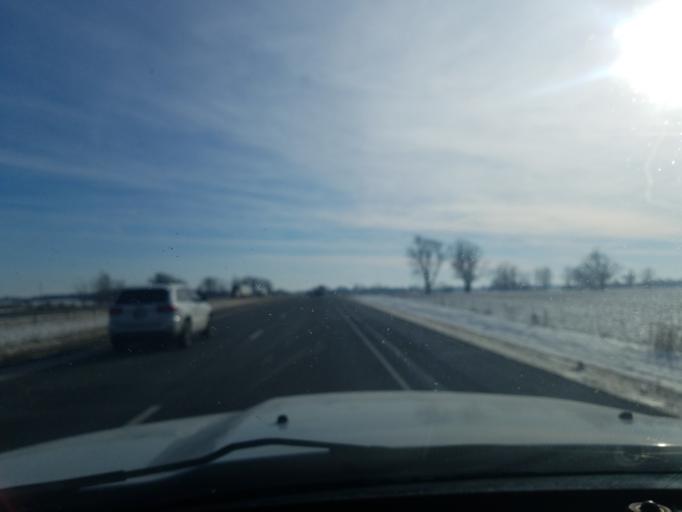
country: US
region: Indiana
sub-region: Grant County
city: Fairmount
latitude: 40.3447
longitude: -85.5590
